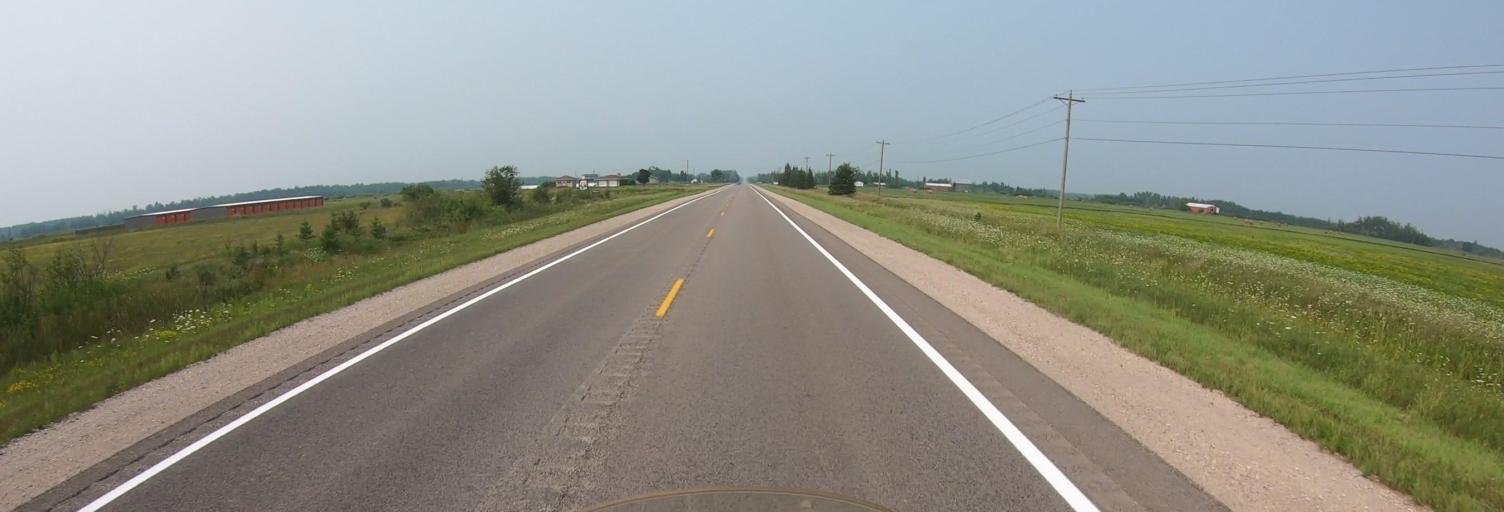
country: US
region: Michigan
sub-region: Chippewa County
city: Sault Ste. Marie
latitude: 46.1680
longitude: -84.3635
